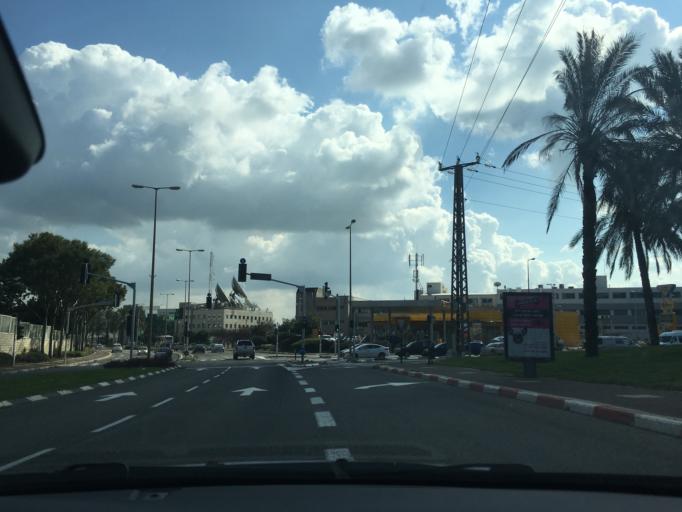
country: IL
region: Central District
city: Kfar Saba
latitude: 32.1794
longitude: 34.9282
